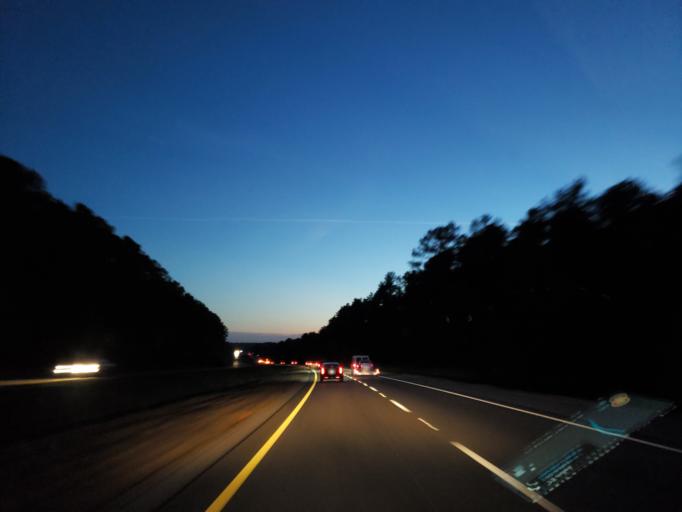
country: US
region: Mississippi
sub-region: Clarke County
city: Stonewall
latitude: 32.2362
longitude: -88.8314
